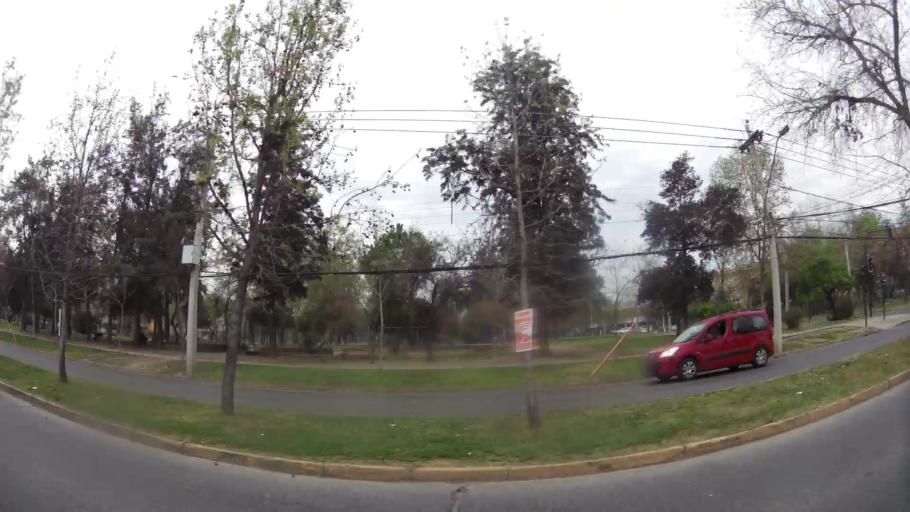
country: CL
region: Santiago Metropolitan
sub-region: Provincia de Santiago
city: Villa Presidente Frei, Nunoa, Santiago, Chile
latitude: -33.4712
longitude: -70.5907
